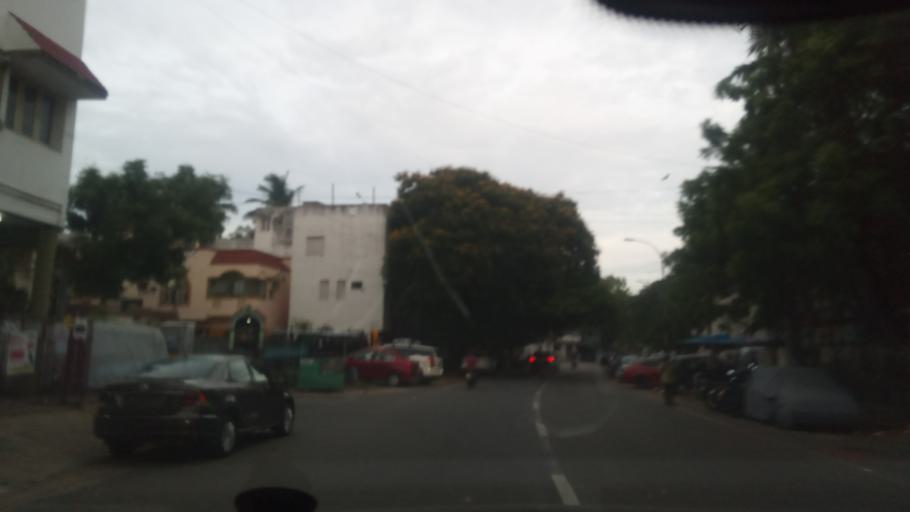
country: IN
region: Tamil Nadu
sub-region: Chennai
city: Chetput
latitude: 13.0411
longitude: 80.2164
